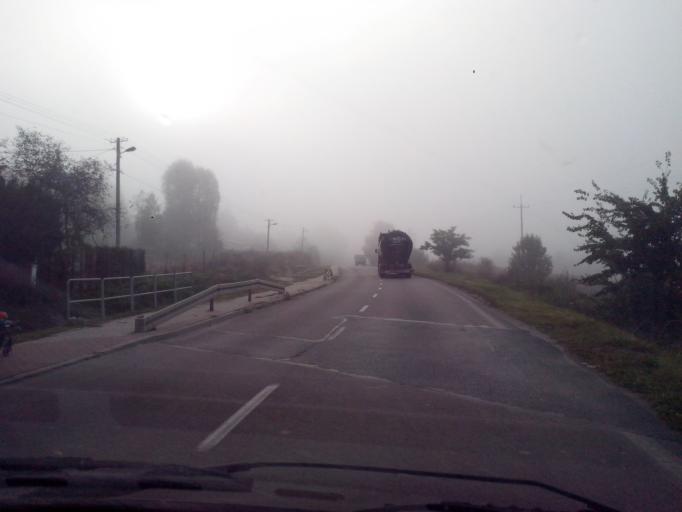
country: PL
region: Subcarpathian Voivodeship
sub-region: Powiat przemyski
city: Krasiczyn
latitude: 49.8055
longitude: 22.7066
